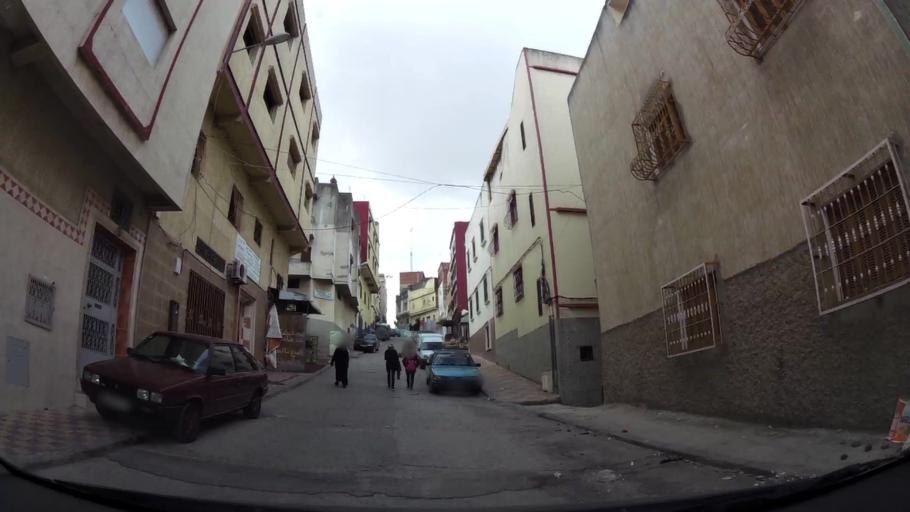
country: MA
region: Tanger-Tetouan
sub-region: Tanger-Assilah
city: Tangier
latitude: 35.7696
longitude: -5.8253
